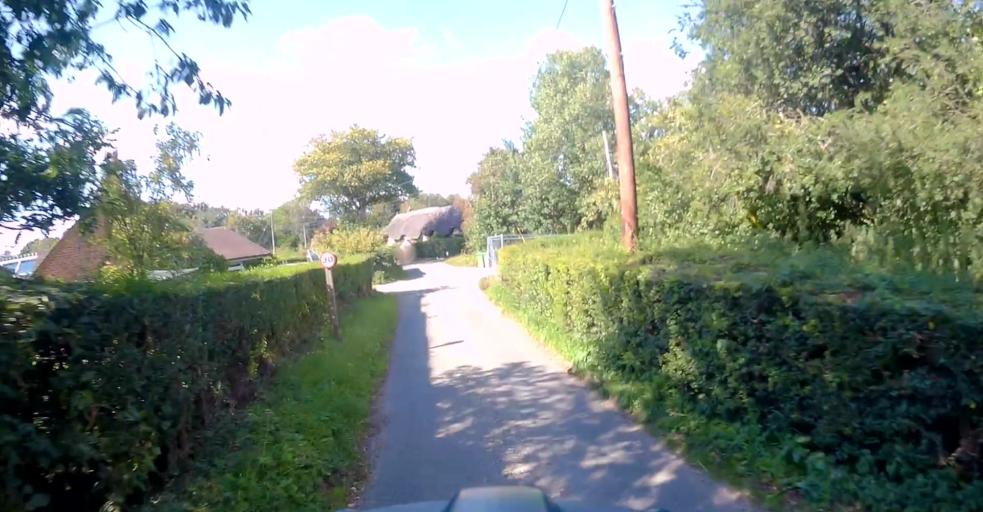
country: GB
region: England
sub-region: Hampshire
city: Four Marks
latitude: 51.1687
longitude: -1.0914
